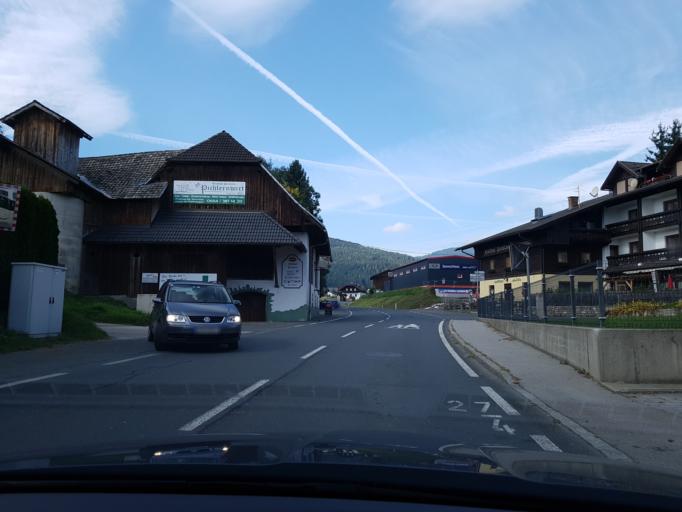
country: AT
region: Carinthia
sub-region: Politischer Bezirk Feldkirchen
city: Feldkirchen in Karnten
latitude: 46.7367
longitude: 14.0634
